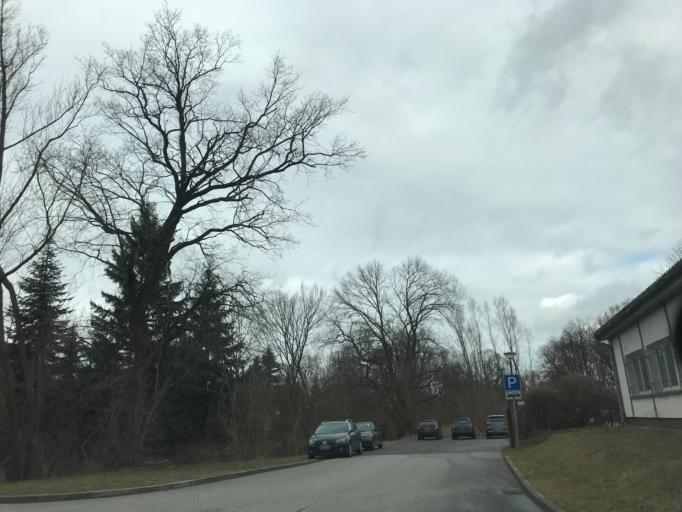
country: DE
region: Brandenburg
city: Luebben
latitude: 51.9428
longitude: 13.9011
